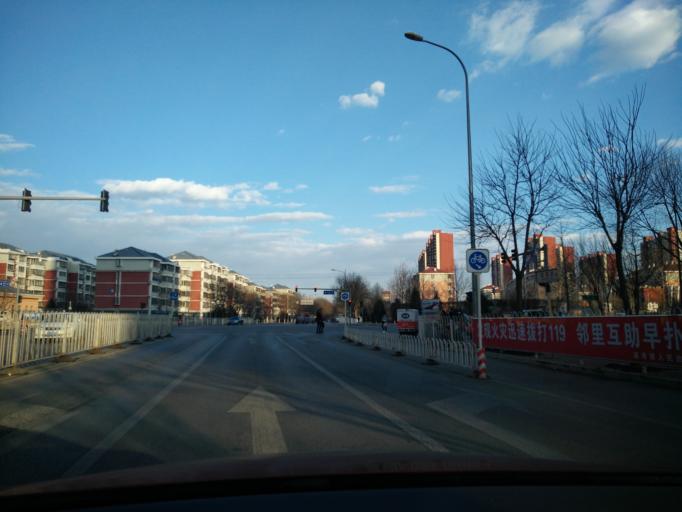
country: CN
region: Beijing
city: Yinghai
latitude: 39.7601
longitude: 116.4916
